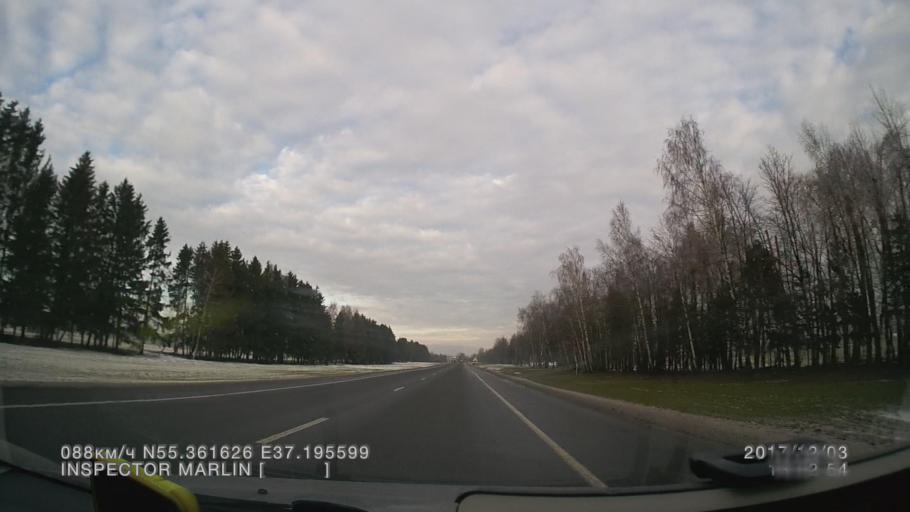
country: RU
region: Moskovskaya
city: Troitsk
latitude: 55.3616
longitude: 37.1956
